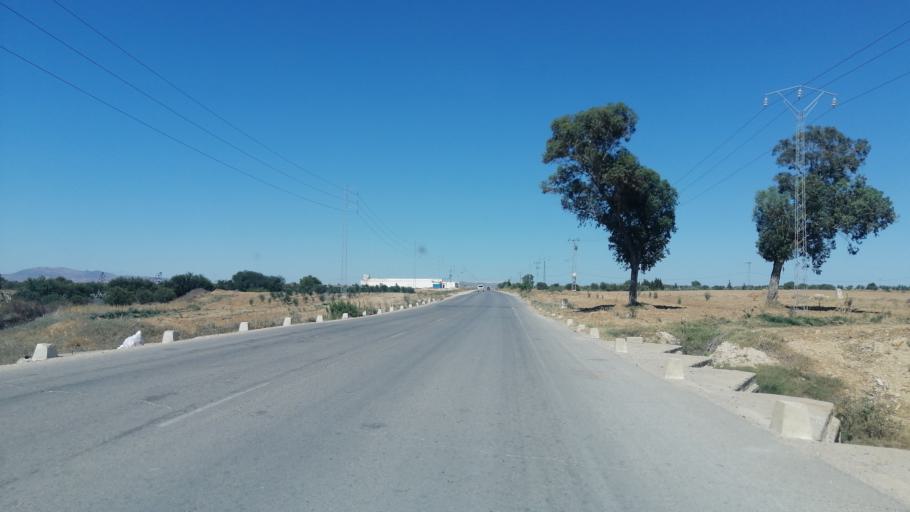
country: TN
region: Al Qayrawan
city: Sbikha
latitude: 36.1280
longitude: 10.1011
